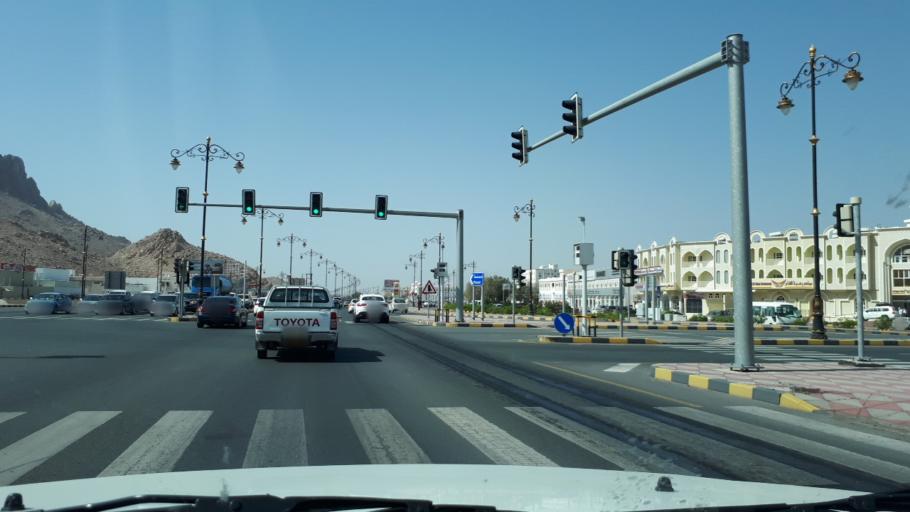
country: OM
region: Muhafazat ad Dakhiliyah
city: Nizwa
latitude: 22.9069
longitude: 57.5340
